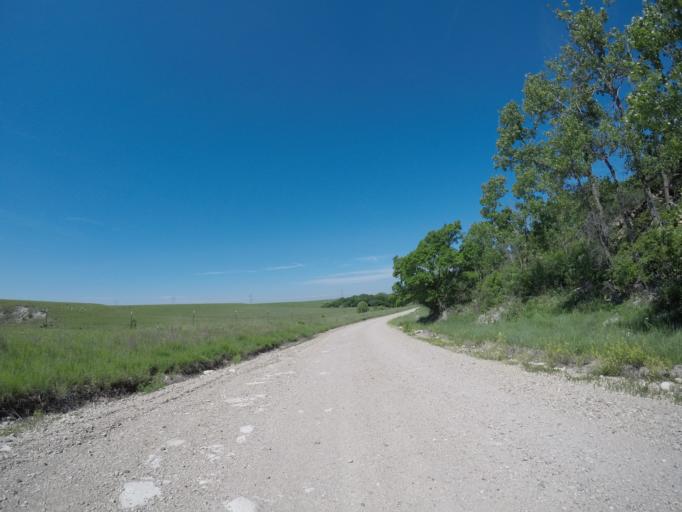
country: US
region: Kansas
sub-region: Wabaunsee County
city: Alma
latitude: 39.0003
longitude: -96.1846
